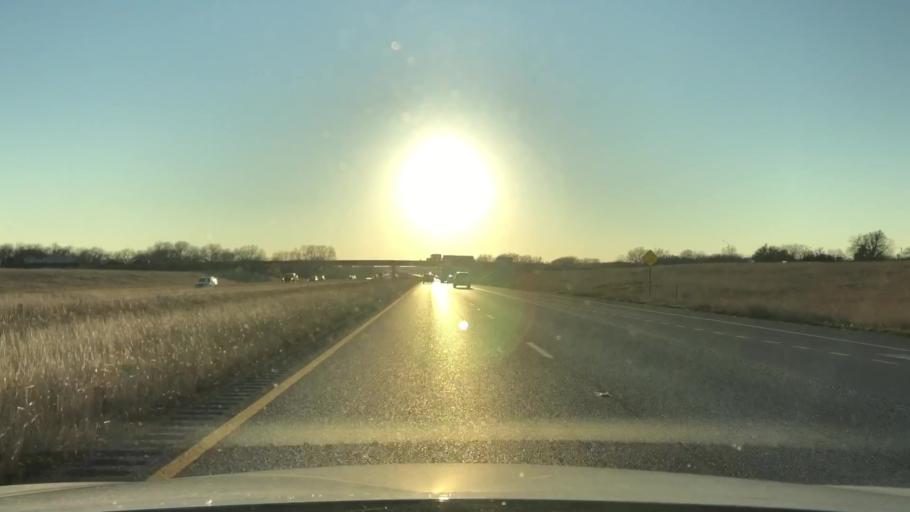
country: US
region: Texas
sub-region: Guadalupe County
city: McQueeney
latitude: 29.5732
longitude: -98.0121
